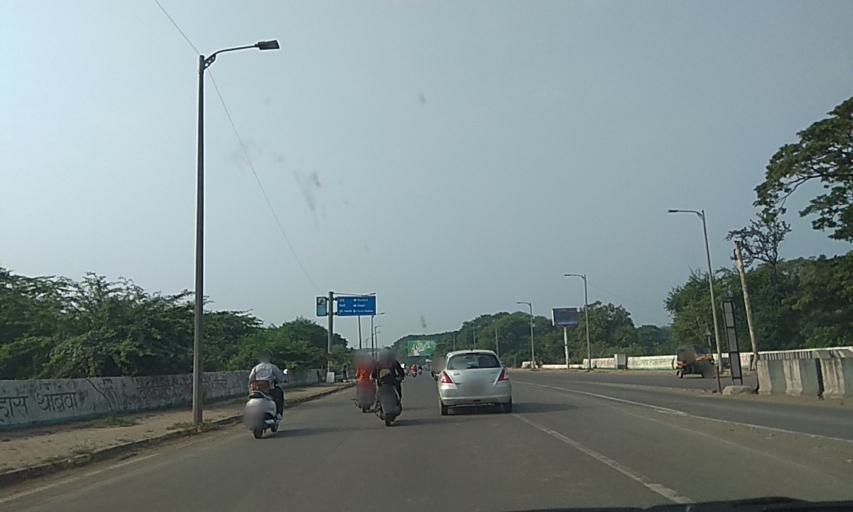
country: IN
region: Maharashtra
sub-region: Pune Division
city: Shivaji Nagar
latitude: 18.5363
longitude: 73.8623
